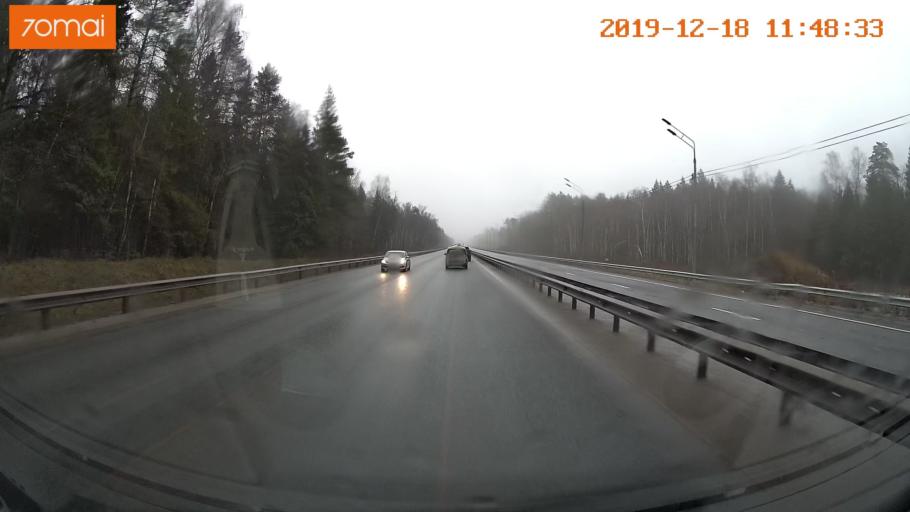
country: RU
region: Moskovskaya
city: Yershovo
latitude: 55.7691
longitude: 36.9044
